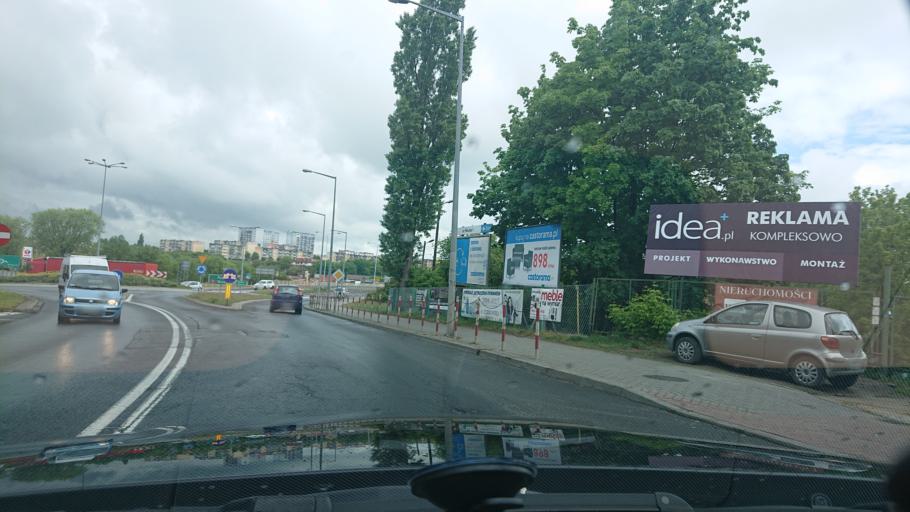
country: PL
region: Greater Poland Voivodeship
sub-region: Powiat gnieznienski
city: Gniezno
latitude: 52.5420
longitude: 17.6046
